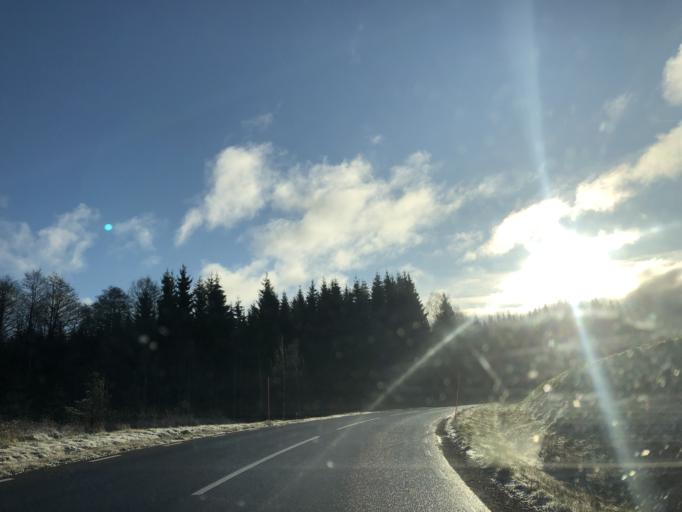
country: SE
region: Vaestra Goetaland
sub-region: Tranemo Kommun
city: Limmared
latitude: 57.6298
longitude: 13.4529
